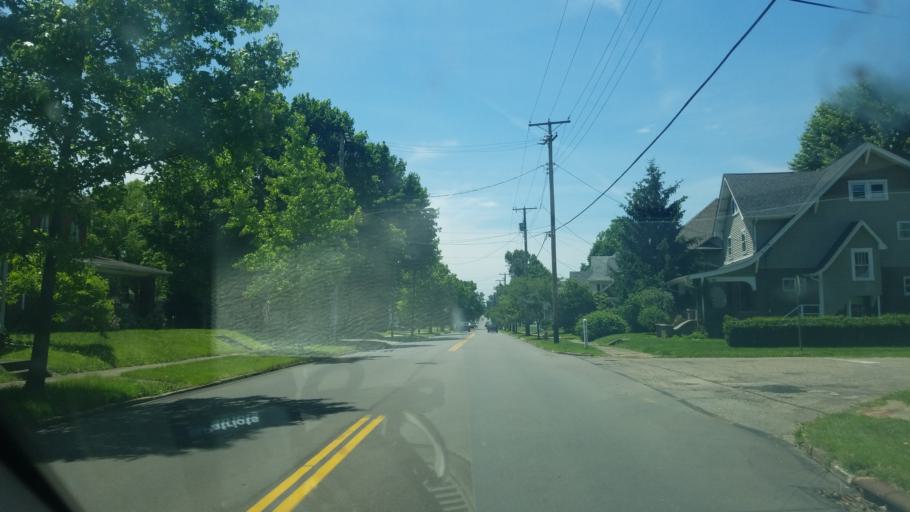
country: US
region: Ohio
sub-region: Stark County
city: Louisville
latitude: 40.8388
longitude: -81.2476
